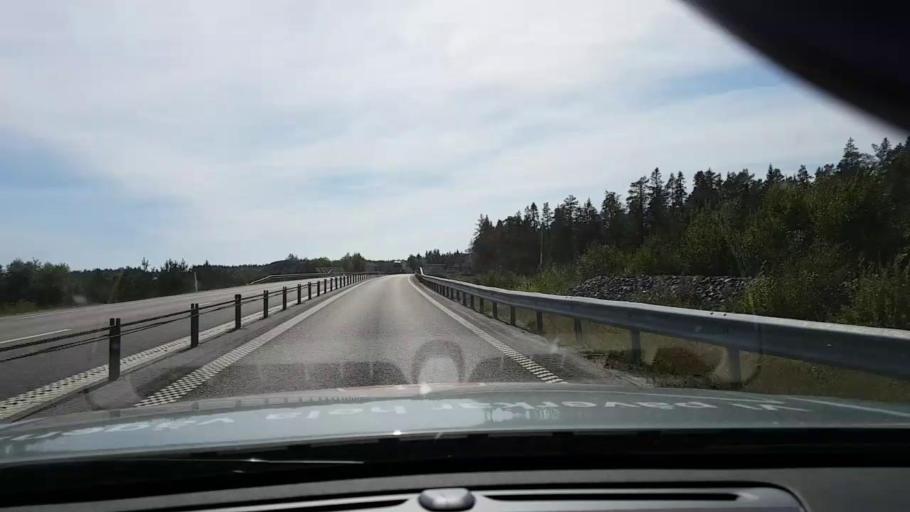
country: SE
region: Vaesternorrland
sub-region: OErnskoeldsviks Kommun
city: Husum
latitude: 63.3696
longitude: 19.1882
